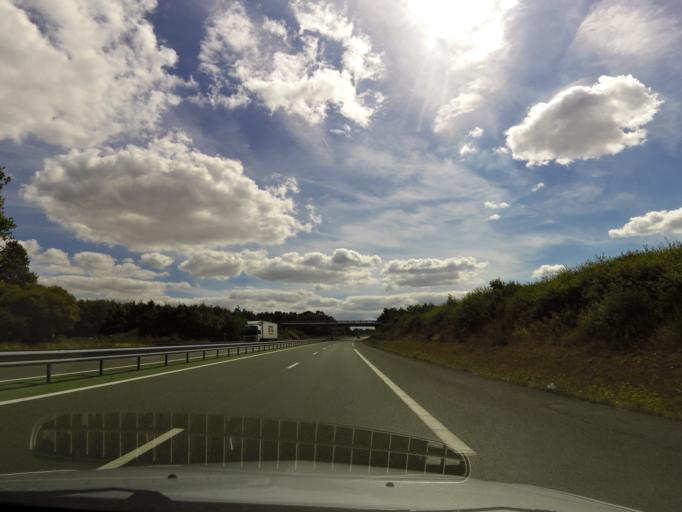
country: FR
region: Pays de la Loire
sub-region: Departement de la Vendee
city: Les Essarts
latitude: 46.7439
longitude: -1.2669
